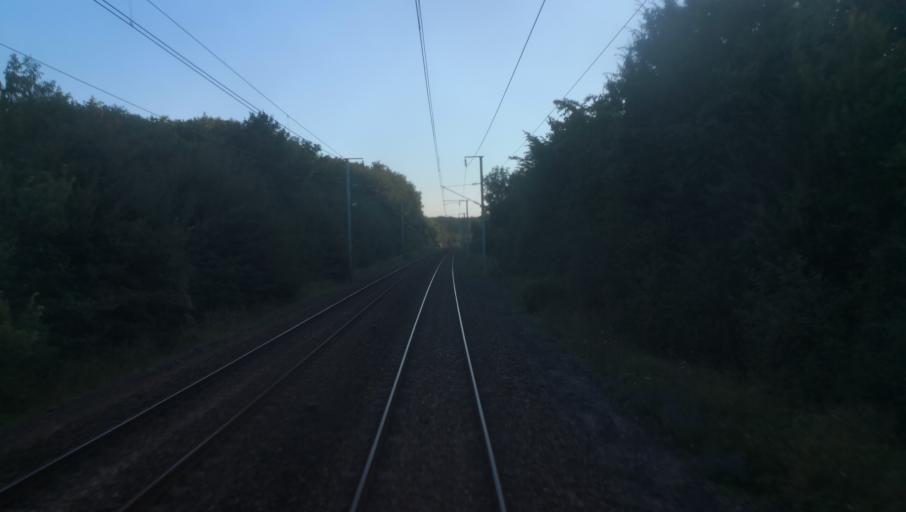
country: FR
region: Haute-Normandie
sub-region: Departement de l'Eure
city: Claville
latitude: 48.9811
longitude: 1.0198
